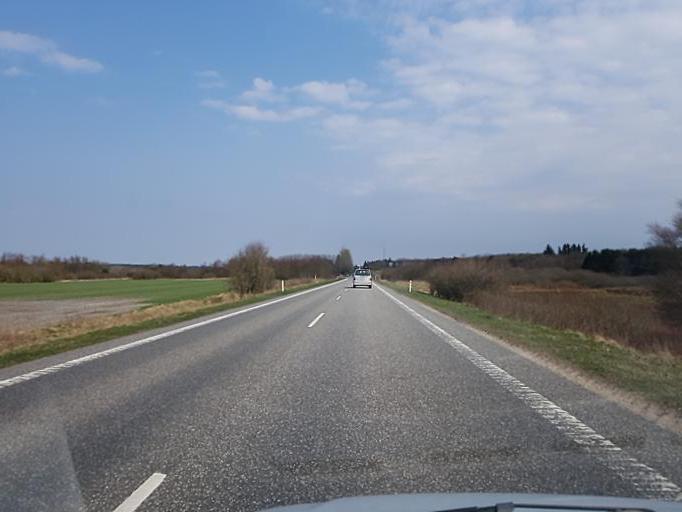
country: DK
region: Central Jutland
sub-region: Ringkobing-Skjern Kommune
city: Tarm
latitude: 55.8558
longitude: 8.4974
